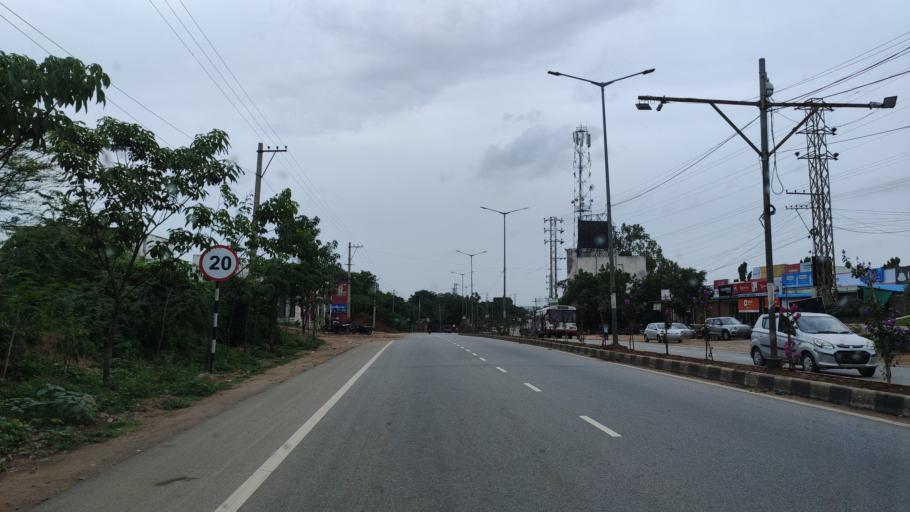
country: IN
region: Telangana
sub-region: Rangareddi
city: Secunderabad
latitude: 17.5939
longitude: 78.5696
